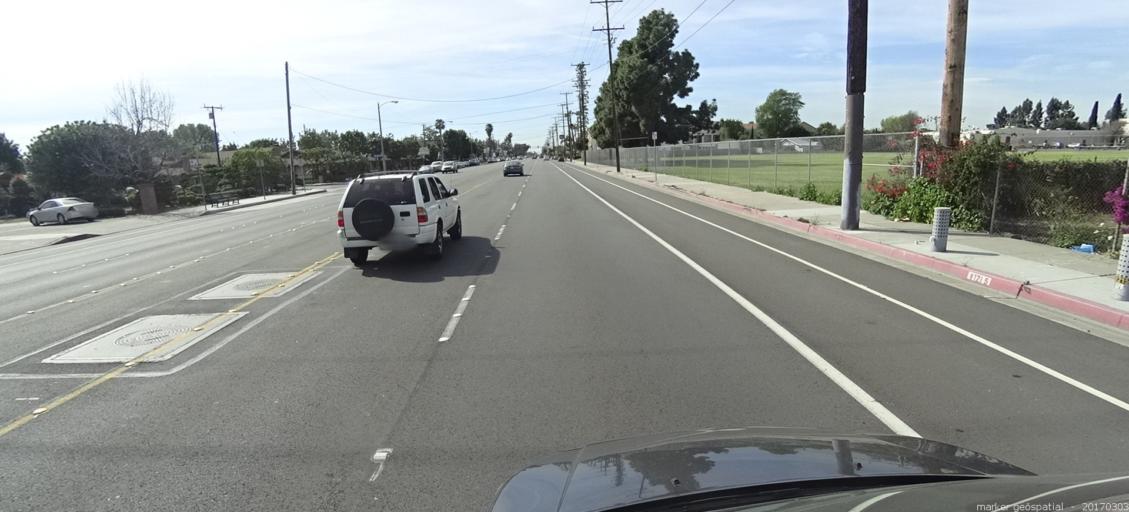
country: US
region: California
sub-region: Orange County
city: Stanton
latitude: 33.8176
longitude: -117.9809
